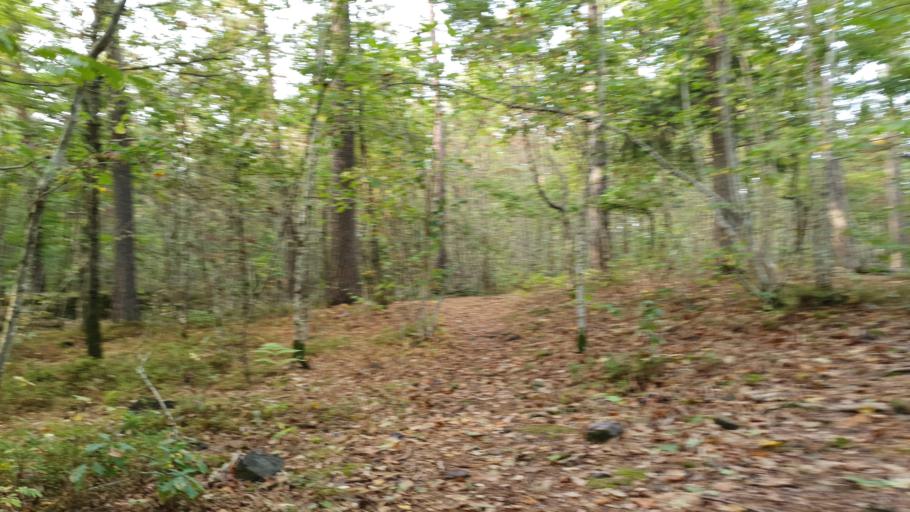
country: NO
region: Vestfold
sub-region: Tonsberg
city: Tonsberg
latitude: 59.2822
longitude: 10.4244
